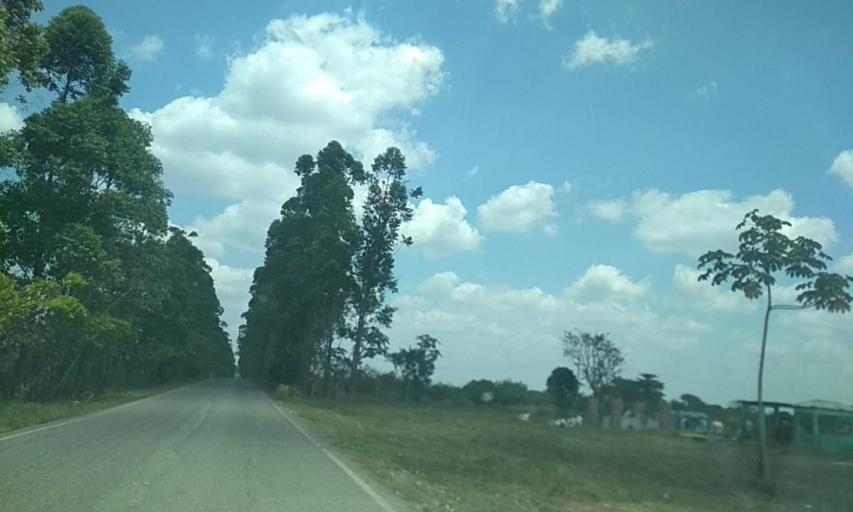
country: MX
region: Tabasco
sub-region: Huimanguillo
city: Francisco Rueda
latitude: 17.7648
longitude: -93.7923
